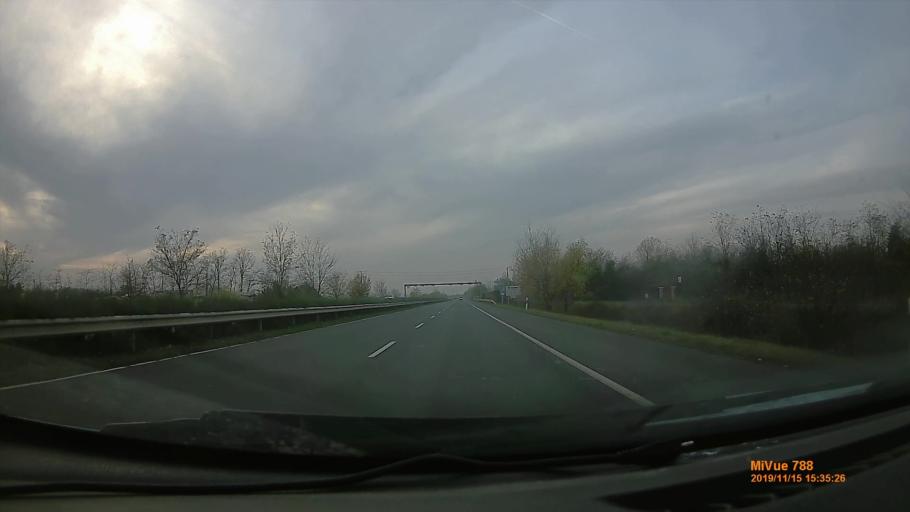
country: HU
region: Bekes
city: Gyula
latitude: 46.6546
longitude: 21.2288
